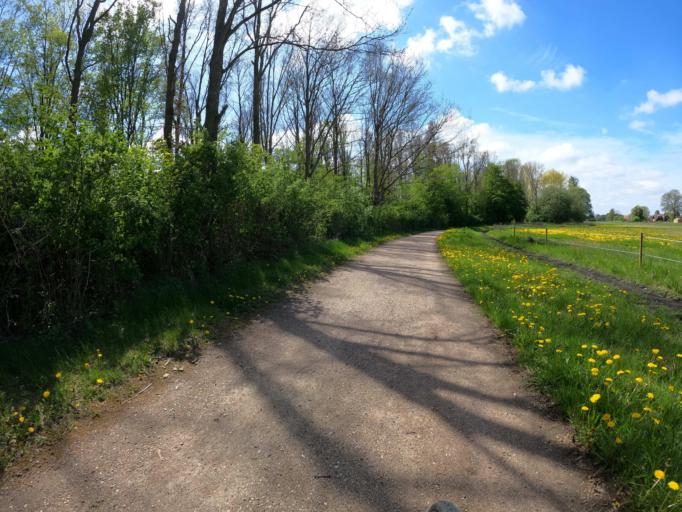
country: DK
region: Capital Region
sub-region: Ishoj Kommune
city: Ishoj
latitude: 55.6246
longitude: 12.3560
